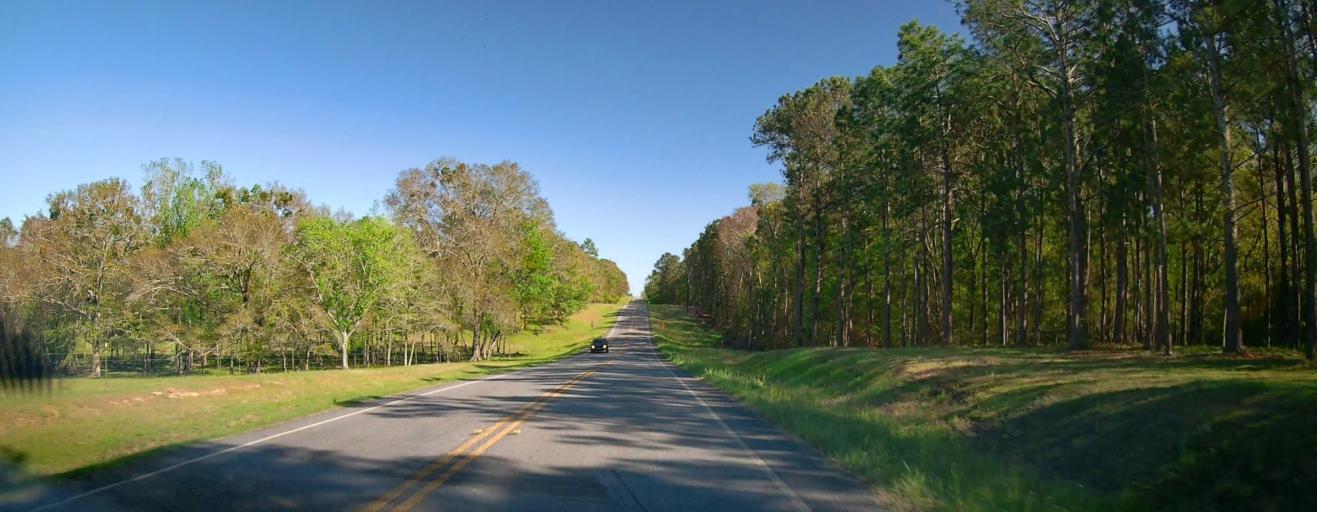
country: US
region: Georgia
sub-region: Wilcox County
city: Rochelle
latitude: 32.0070
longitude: -83.4875
